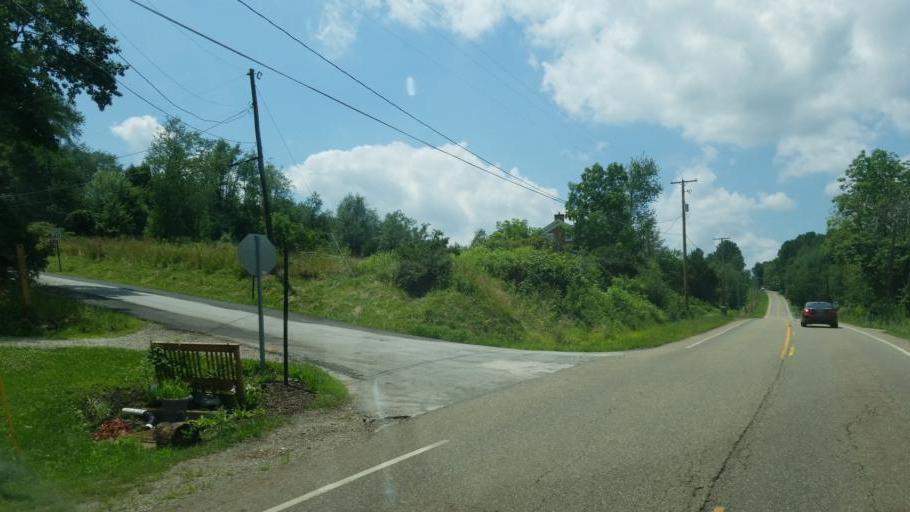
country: US
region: Ohio
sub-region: Stark County
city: East Canton
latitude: 40.7949
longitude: -81.2519
